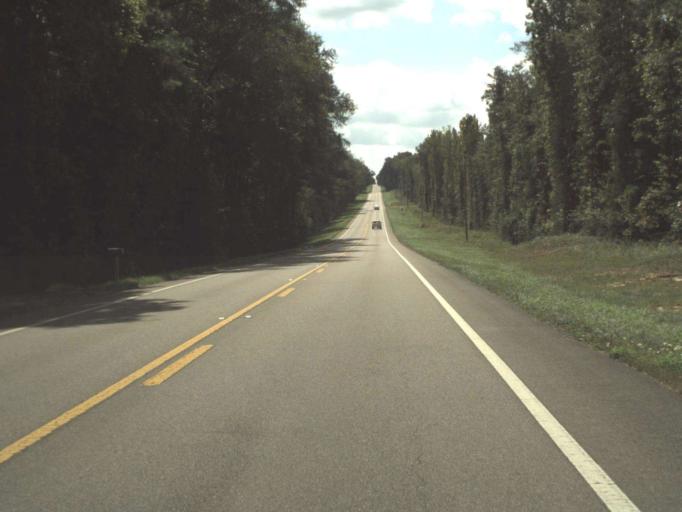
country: US
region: Florida
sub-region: Walton County
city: DeFuniak Springs
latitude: 30.6814
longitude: -85.9365
